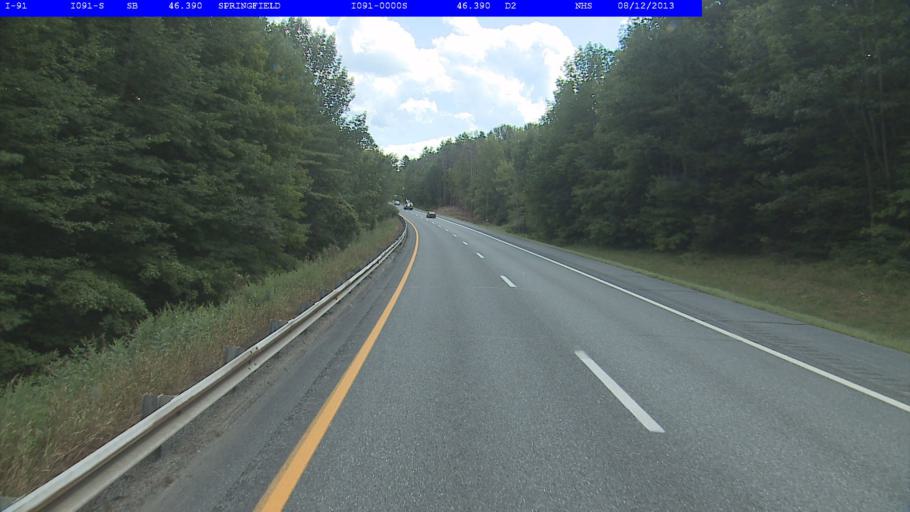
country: US
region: Vermont
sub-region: Windsor County
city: Springfield
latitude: 43.3323
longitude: -72.4215
